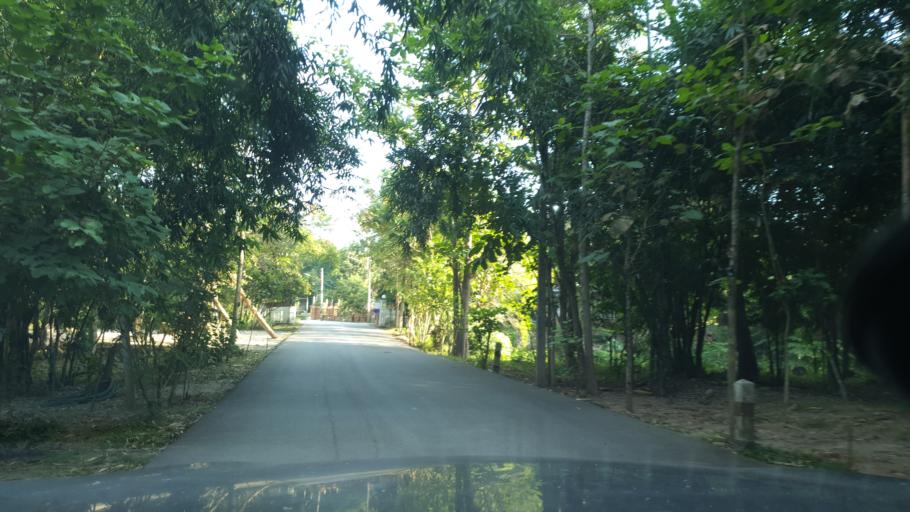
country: TH
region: Chiang Mai
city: Chiang Mai
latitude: 18.8277
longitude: 98.9525
